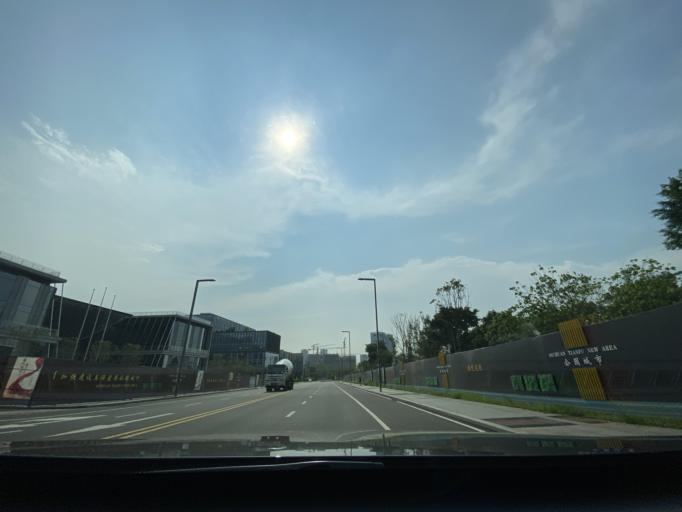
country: CN
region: Sichuan
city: Dongsheng
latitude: 30.3934
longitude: 104.0812
